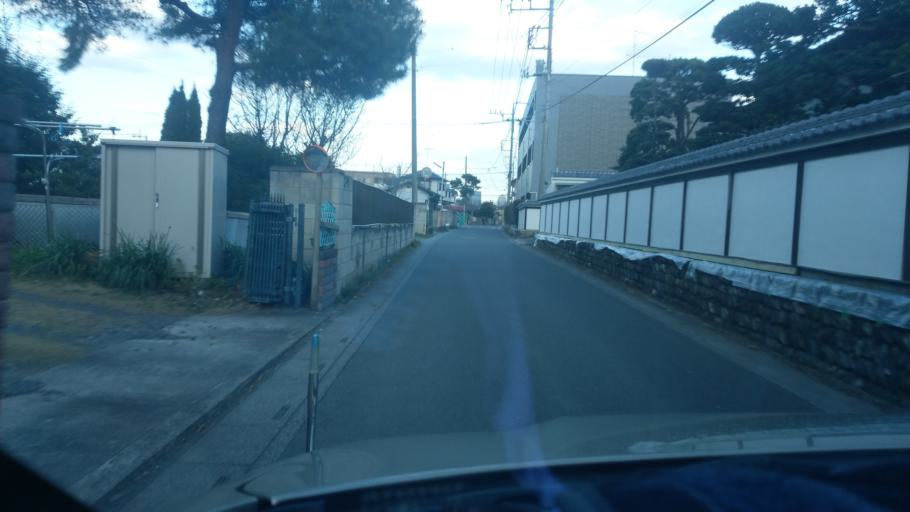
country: JP
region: Saitama
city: Yono
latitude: 35.8879
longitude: 139.5999
